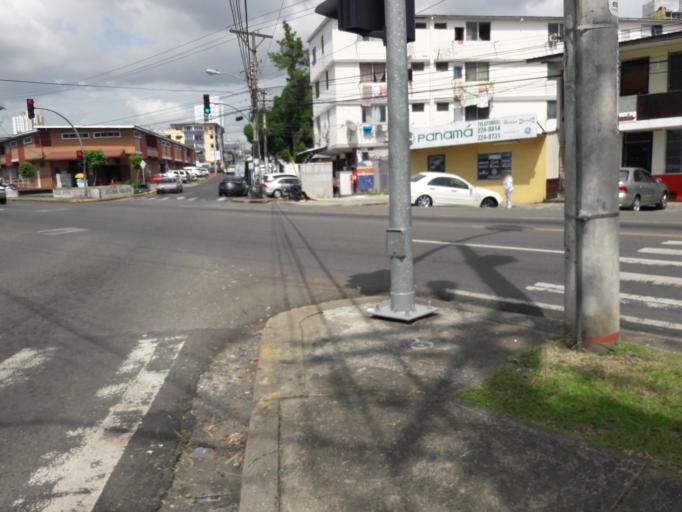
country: PA
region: Panama
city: Panama
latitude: 9.0072
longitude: -79.5032
